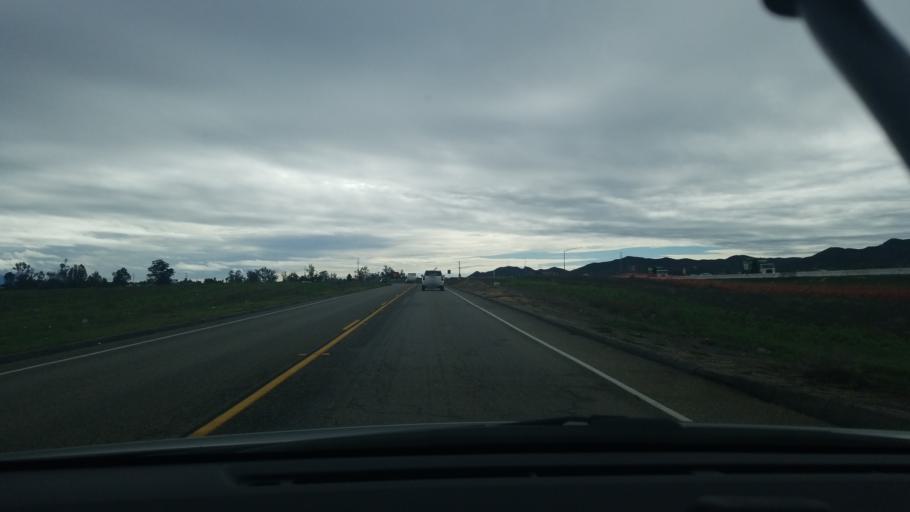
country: US
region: California
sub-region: Riverside County
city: Sun City
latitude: 33.6485
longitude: -117.1704
